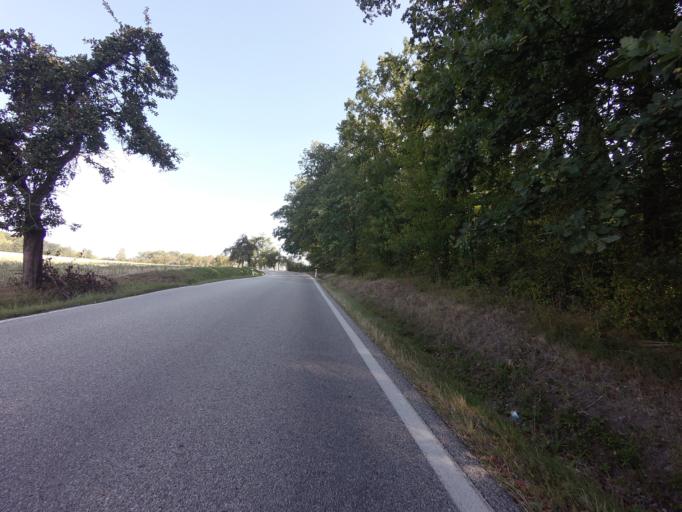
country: CZ
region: Jihocesky
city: Tyn nad Vltavou
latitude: 49.2562
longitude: 14.4175
